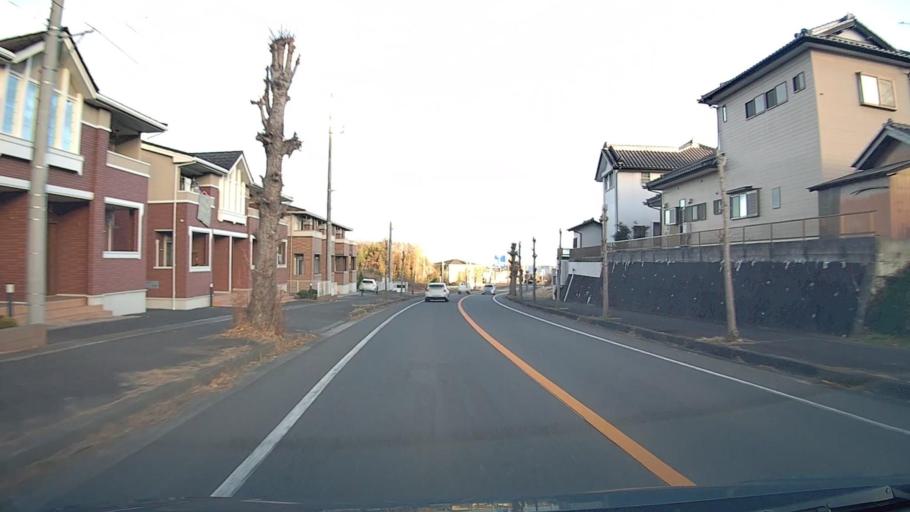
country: JP
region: Ibaraki
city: Kitaibaraki
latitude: 36.8059
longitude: 140.7553
